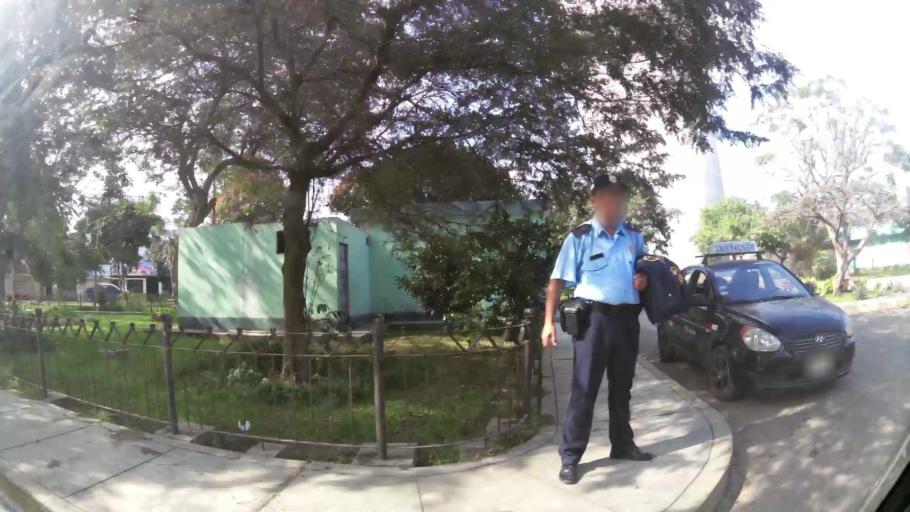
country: PE
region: La Libertad
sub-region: Provincia de Trujillo
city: Trujillo
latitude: -8.1080
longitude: -79.0136
